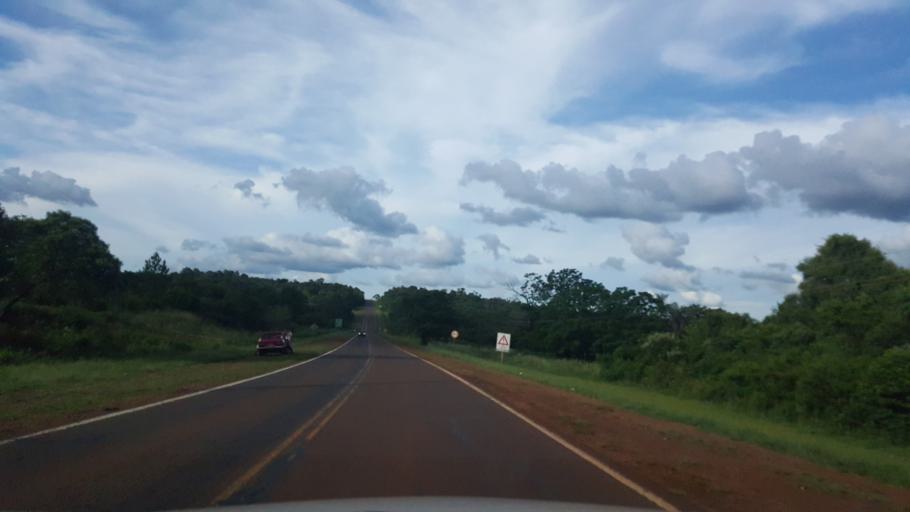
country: AR
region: Misiones
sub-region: Departamento de San Ignacio
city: San Ignacio
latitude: -27.2533
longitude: -55.5237
